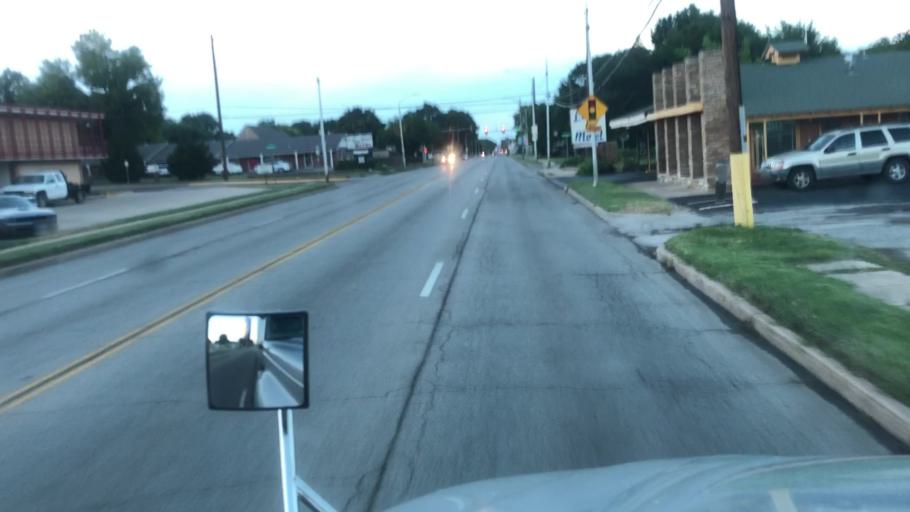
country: US
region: Oklahoma
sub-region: Kay County
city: Ponca City
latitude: 36.7016
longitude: -97.0672
